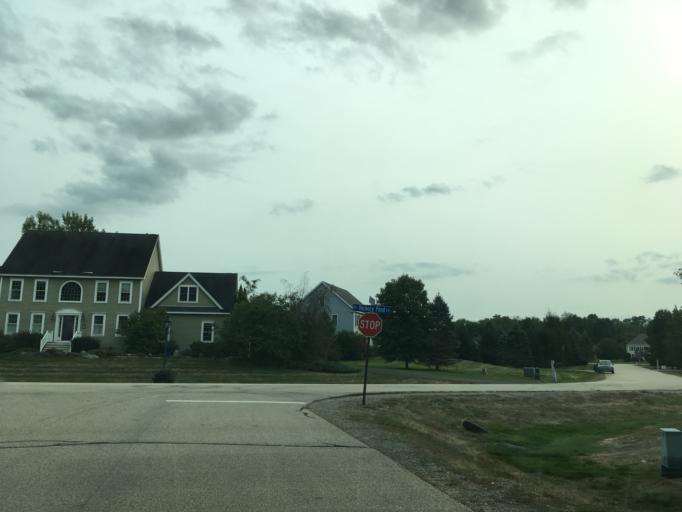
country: US
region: New Hampshire
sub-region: Rockingham County
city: Stratham Station
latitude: 43.0057
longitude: -70.8917
